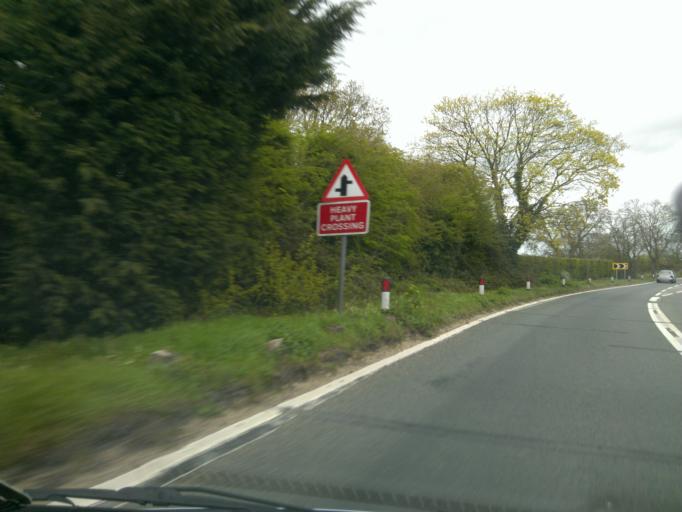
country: GB
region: England
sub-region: Essex
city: Wivenhoe
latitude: 51.8733
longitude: 0.9765
